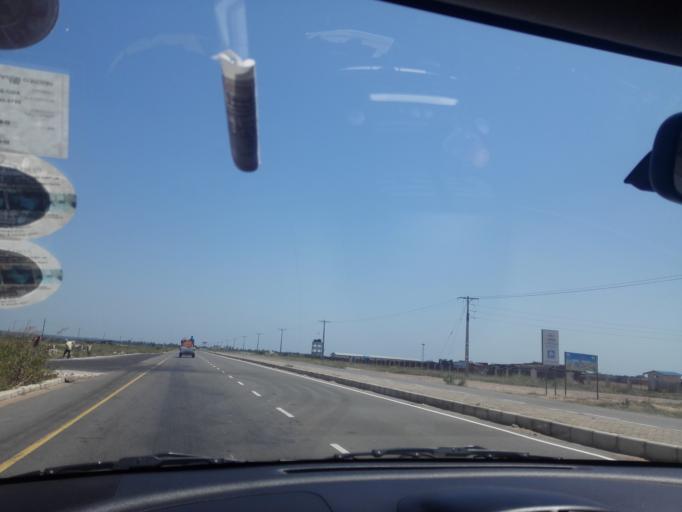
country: MZ
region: Maputo City
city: Maputo
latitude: -25.8372
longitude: 32.6717
